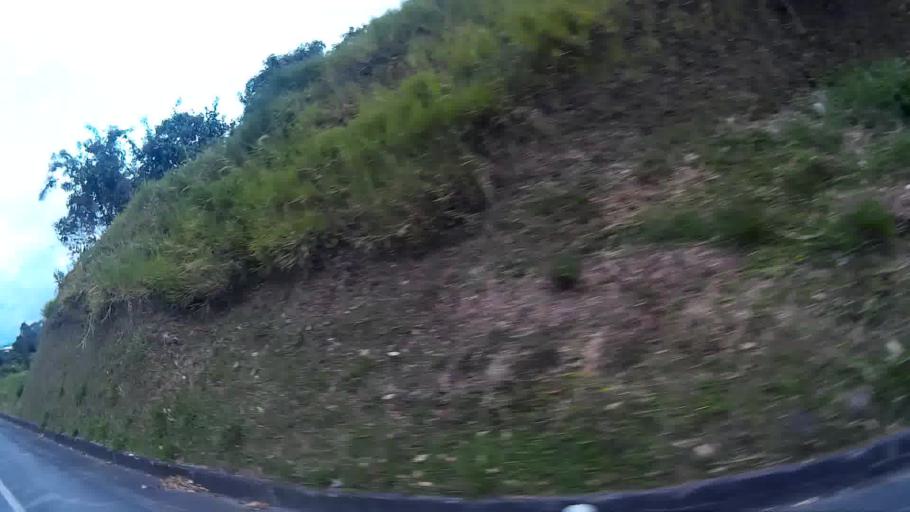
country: CO
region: Quindio
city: Filandia
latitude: 4.7321
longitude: -75.6388
